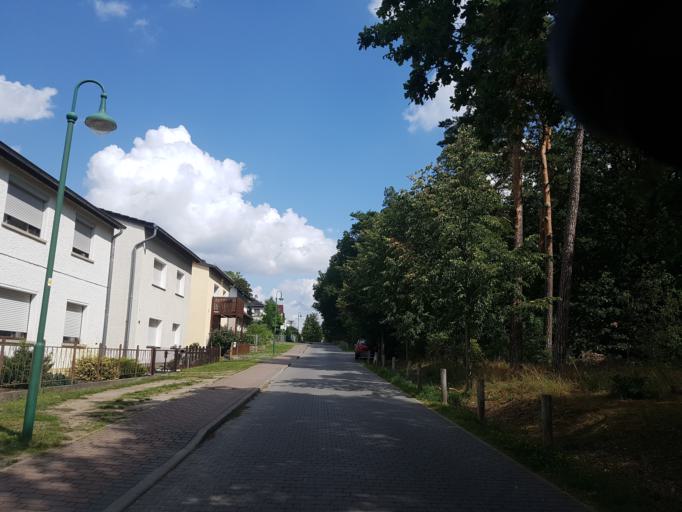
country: DE
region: Brandenburg
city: Gross Kreutz
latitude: 52.3097
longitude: 12.7376
